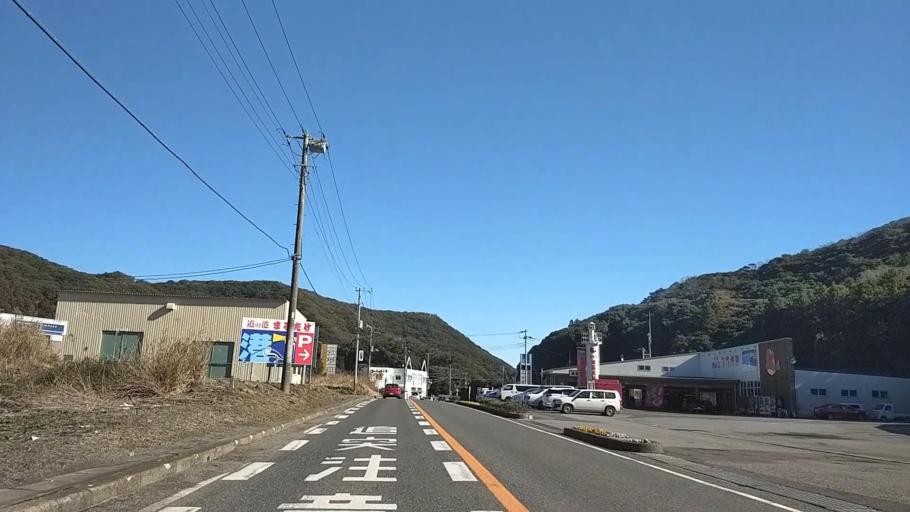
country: JP
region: Chiba
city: Kawaguchi
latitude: 35.1236
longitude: 140.1393
